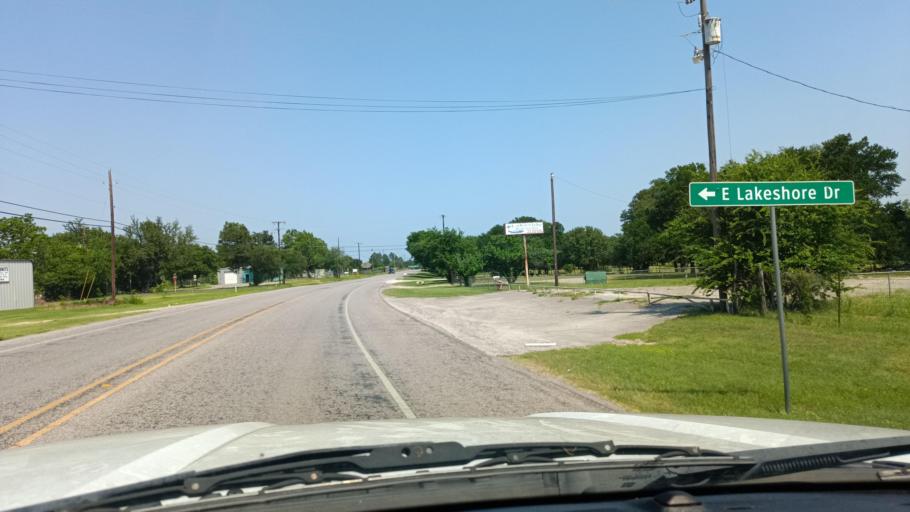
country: US
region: Texas
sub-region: Bell County
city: Morgans Point Resort
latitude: 31.1056
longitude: -97.5057
